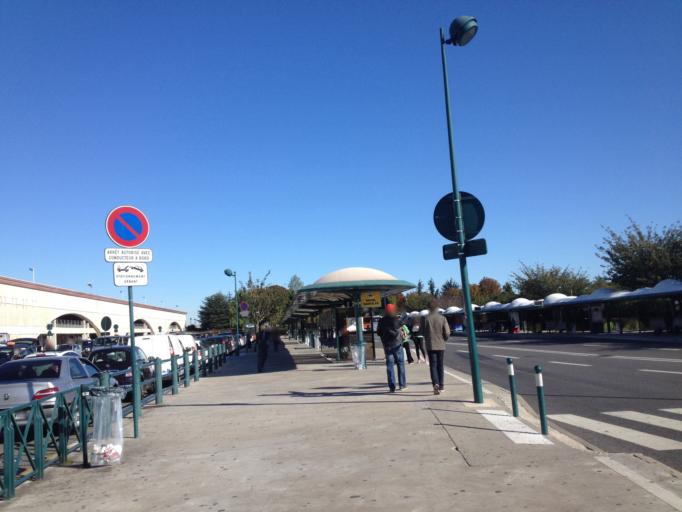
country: FR
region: Ile-de-France
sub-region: Departement de Seine-et-Marne
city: Chessy
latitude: 48.8705
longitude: 2.7836
